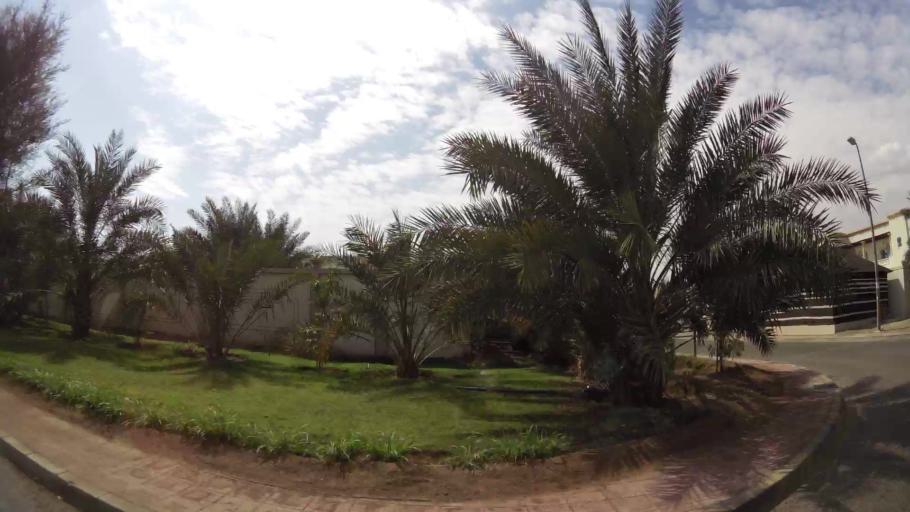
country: AE
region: Abu Dhabi
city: Al Ain
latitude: 24.1949
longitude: 55.7988
